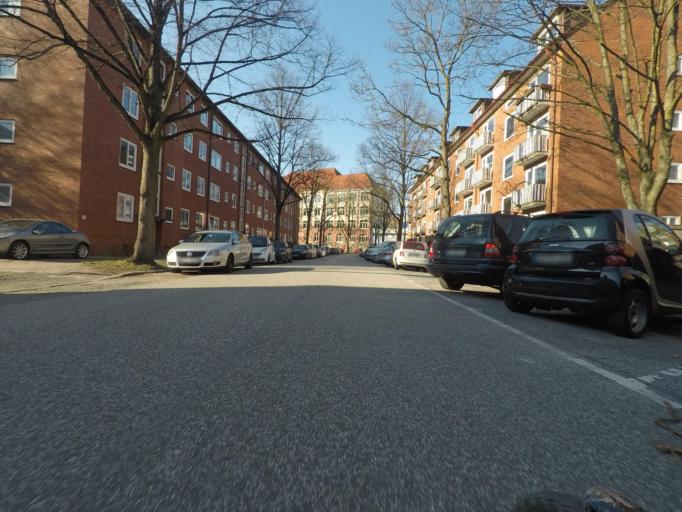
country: DE
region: Hamburg
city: Hamburg
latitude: 53.5786
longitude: 10.0289
